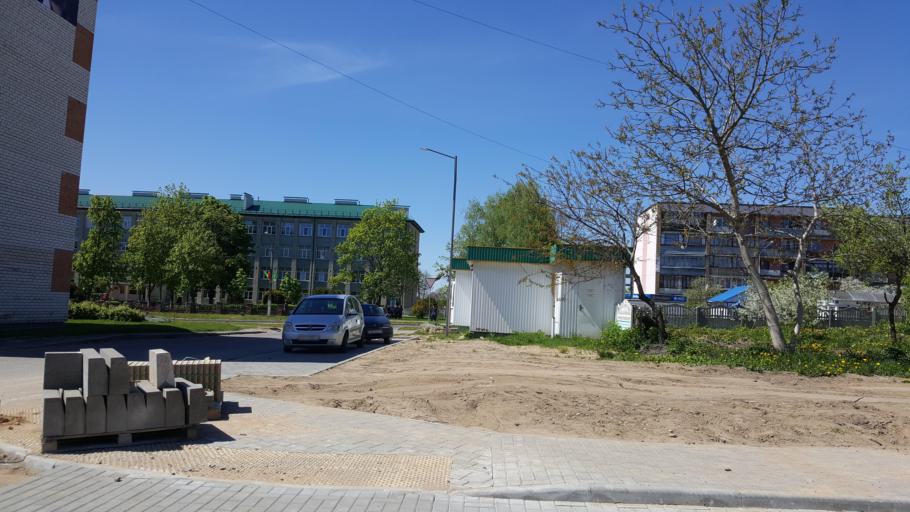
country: BY
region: Brest
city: Kamyanyets
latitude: 52.3946
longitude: 23.8250
